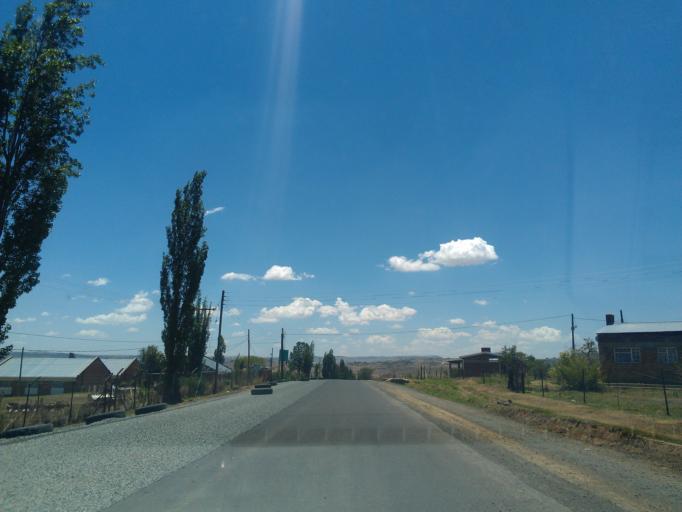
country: LS
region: Berea
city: Teyateyaneng
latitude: -29.1383
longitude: 27.7661
